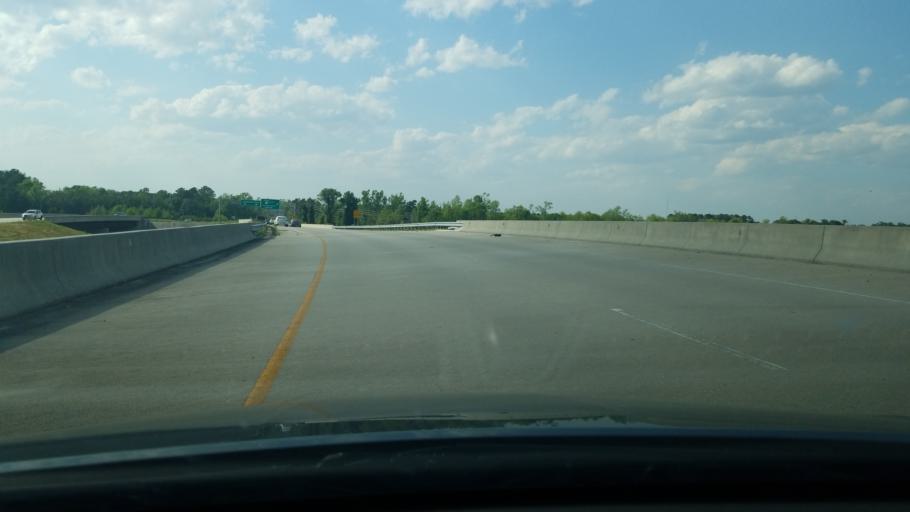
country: US
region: North Carolina
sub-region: Onslow County
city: Pumpkin Center
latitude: 34.7723
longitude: -77.3969
